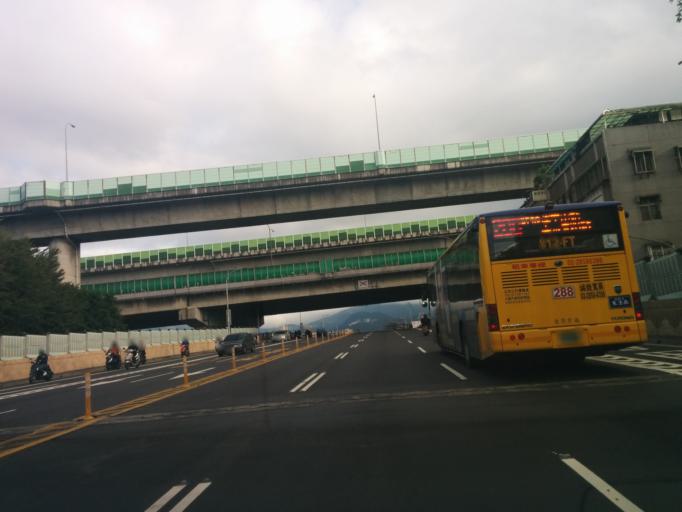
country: TW
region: Taipei
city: Taipei
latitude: 25.0758
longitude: 121.5204
